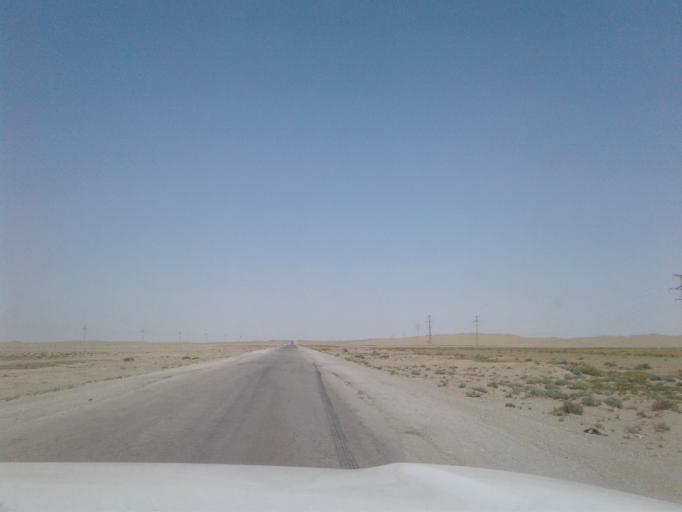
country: TM
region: Balkan
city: Gumdag
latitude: 38.3674
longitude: 54.3852
